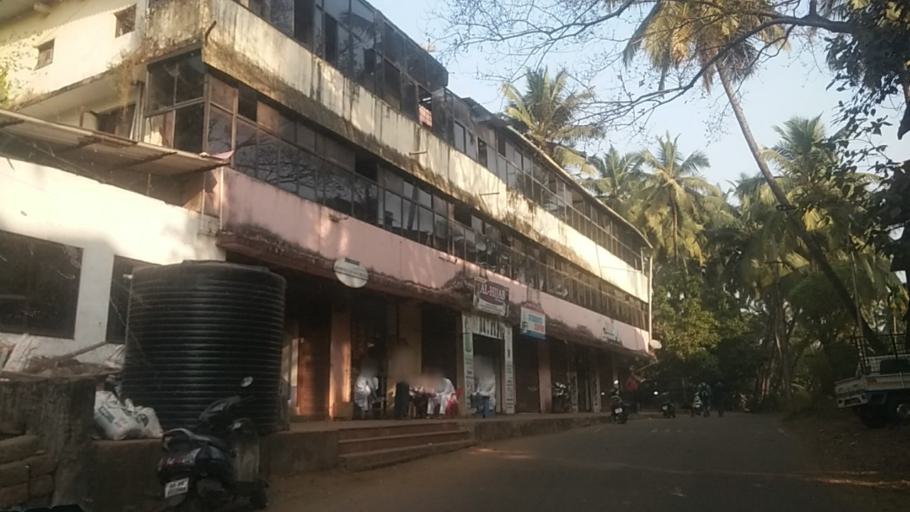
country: IN
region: Goa
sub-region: South Goa
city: Madgaon
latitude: 15.2671
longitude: 73.9571
